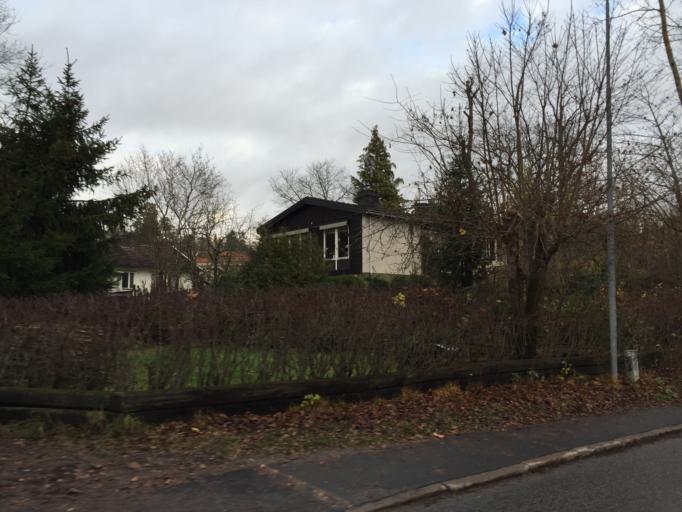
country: SE
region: Stockholm
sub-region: Salems Kommun
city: Ronninge
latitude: 59.1981
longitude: 17.7427
